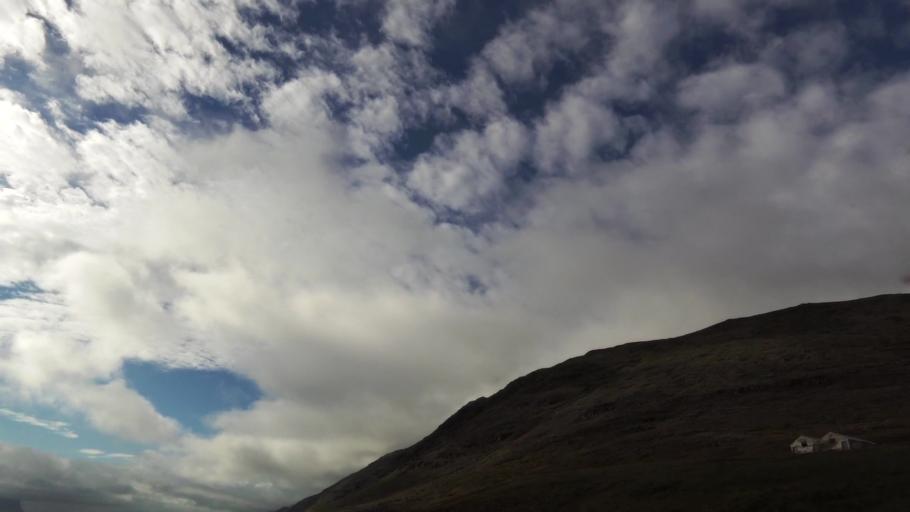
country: IS
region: West
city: Olafsvik
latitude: 65.5515
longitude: -23.8909
